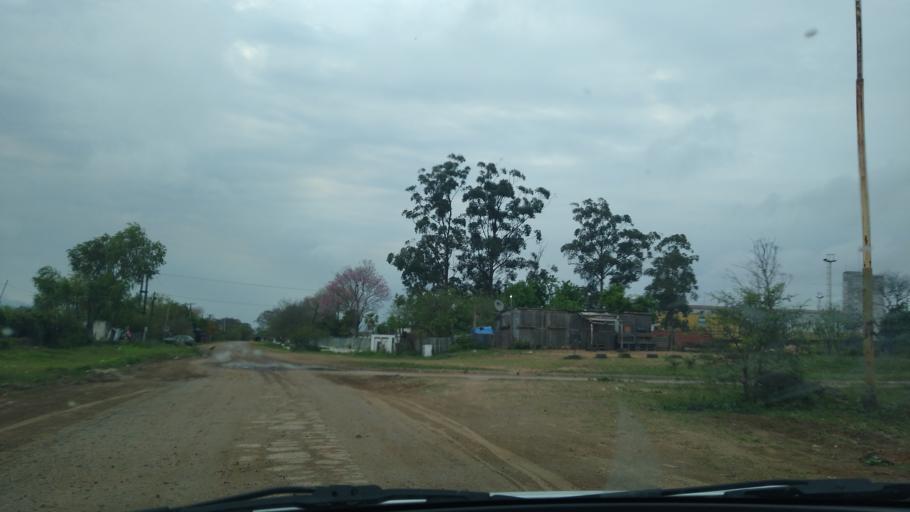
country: AR
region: Chaco
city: Barranqueras
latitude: -27.4680
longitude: -58.9100
